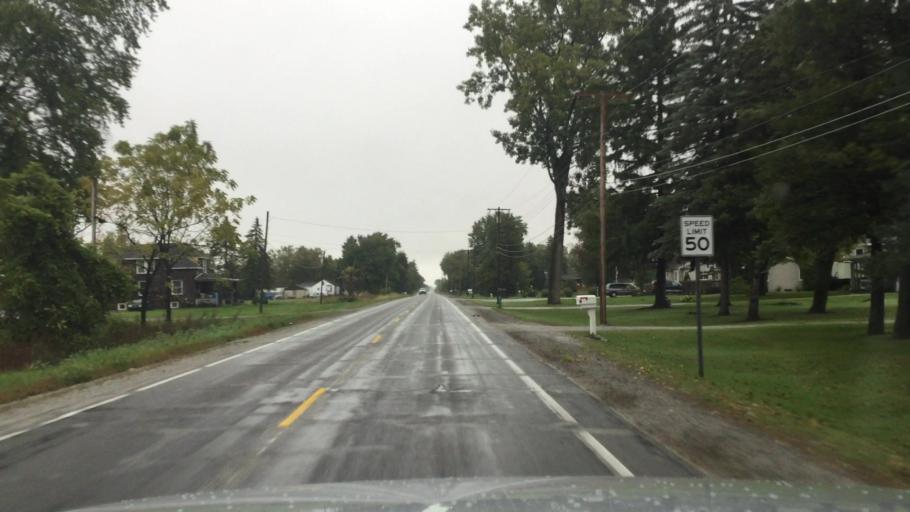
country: US
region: Michigan
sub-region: Saginaw County
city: Bridgeport
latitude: 43.3655
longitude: -83.9350
